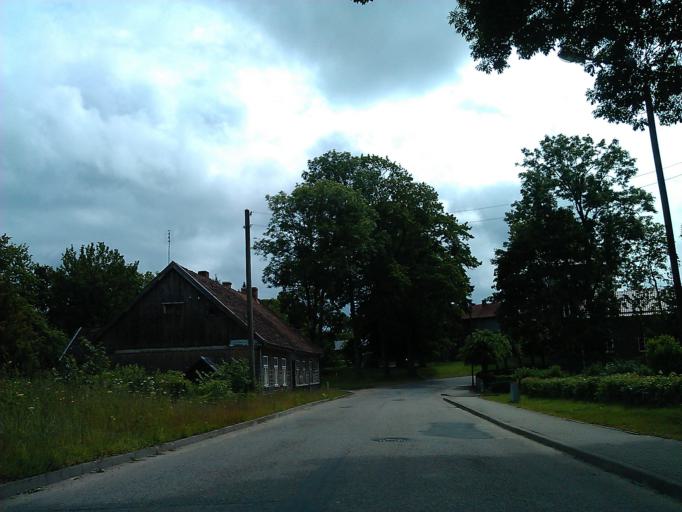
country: LV
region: Aizpute
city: Aizpute
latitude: 56.7248
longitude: 21.6069
